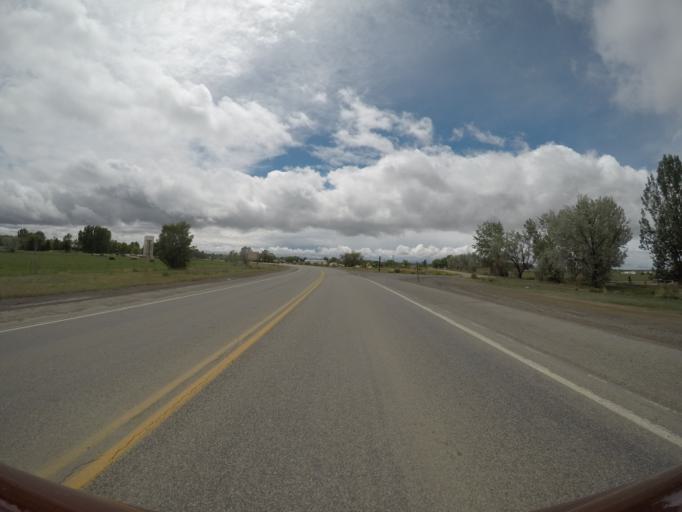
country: US
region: Wyoming
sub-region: Big Horn County
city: Lovell
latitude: 44.8405
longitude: -108.3751
